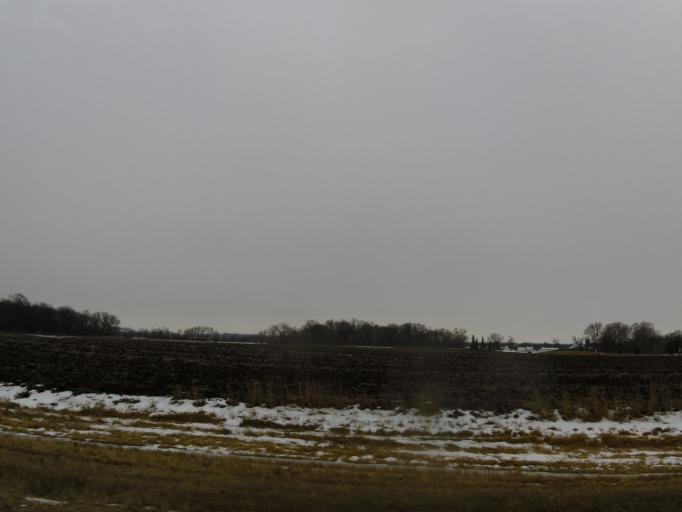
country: US
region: Minnesota
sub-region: Scott County
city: Prior Lake
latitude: 44.6305
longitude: -93.5005
